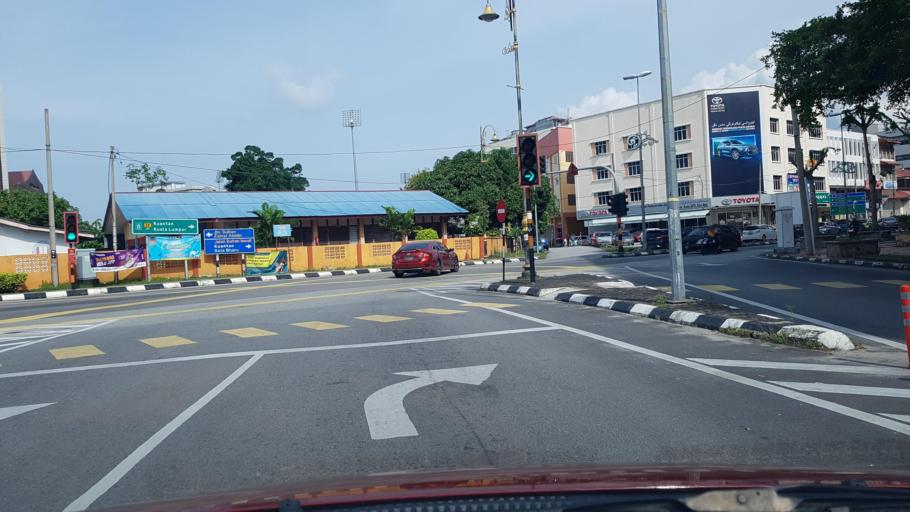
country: MY
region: Terengganu
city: Kuala Terengganu
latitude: 5.3316
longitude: 103.1382
